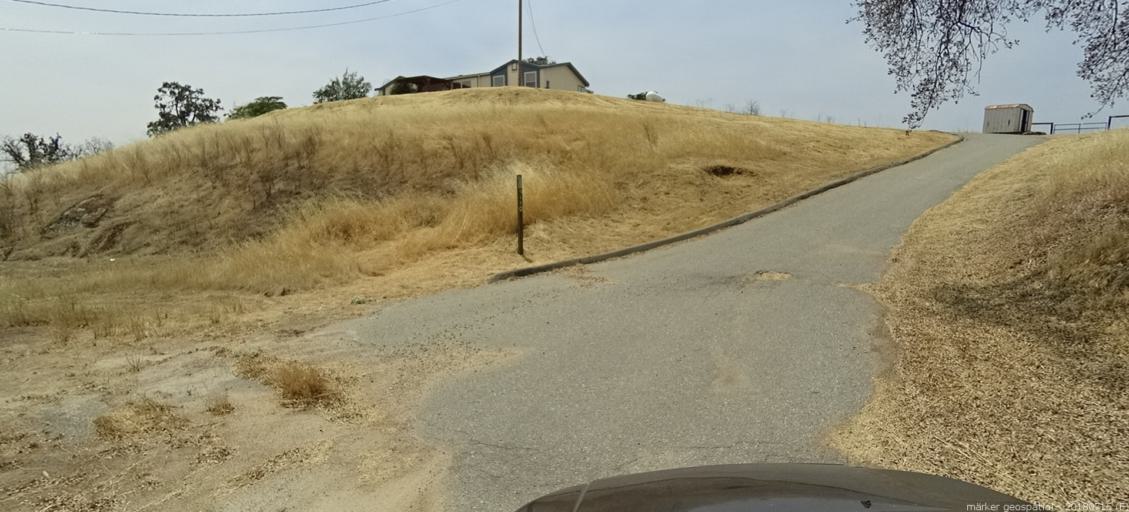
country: US
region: California
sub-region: Madera County
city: Bonadelle Ranchos-Madera Ranchos
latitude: 37.1140
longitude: -119.8958
